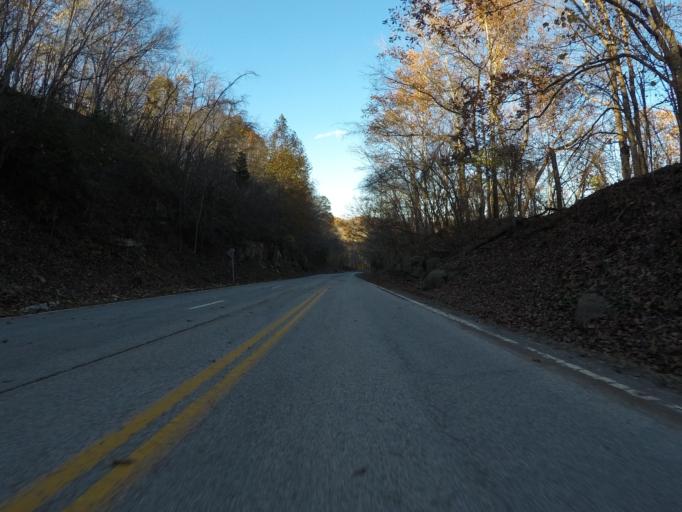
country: US
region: West Virginia
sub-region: Wayne County
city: Ceredo
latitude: 38.3723
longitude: -82.5545
